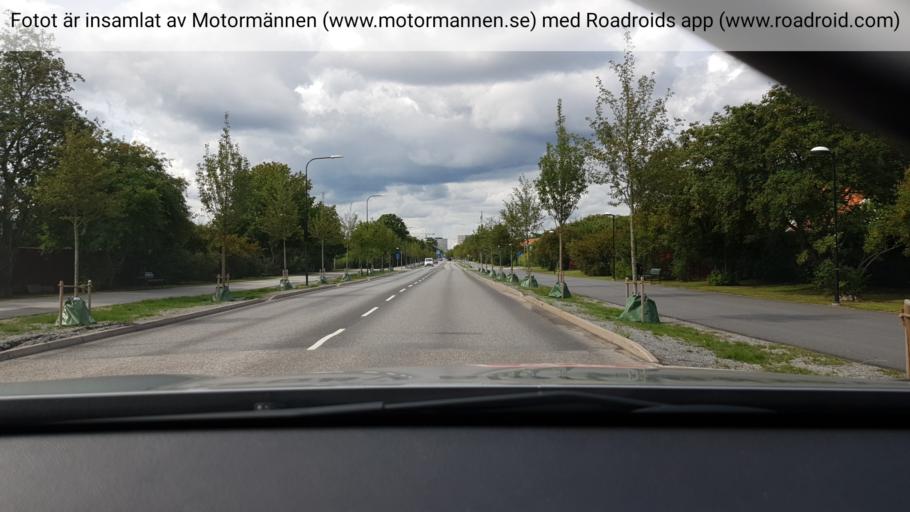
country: SE
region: Stockholm
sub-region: Stockholms Kommun
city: Arsta
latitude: 59.2849
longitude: 18.0681
